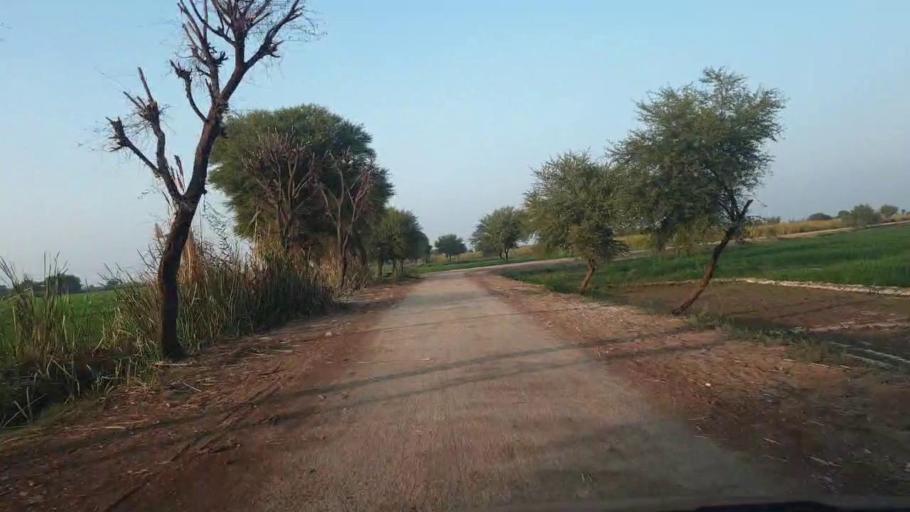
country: PK
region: Sindh
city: Berani
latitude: 25.8363
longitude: 68.7267
